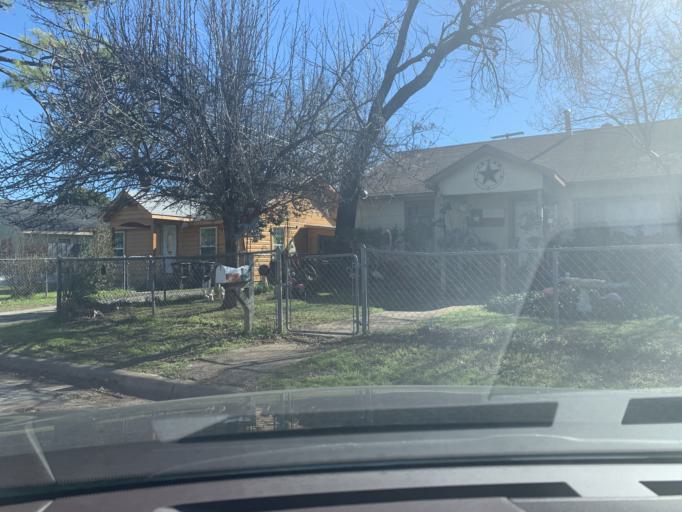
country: US
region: Texas
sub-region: Tarrant County
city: Haltom City
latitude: 32.7640
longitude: -97.2892
